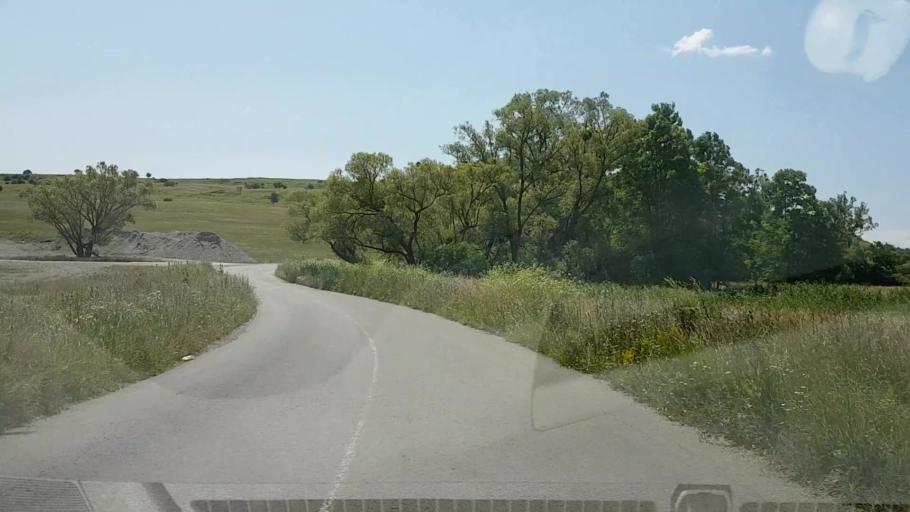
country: RO
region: Brasov
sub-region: Comuna Cincu
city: Cincu
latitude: 45.9523
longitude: 24.7830
